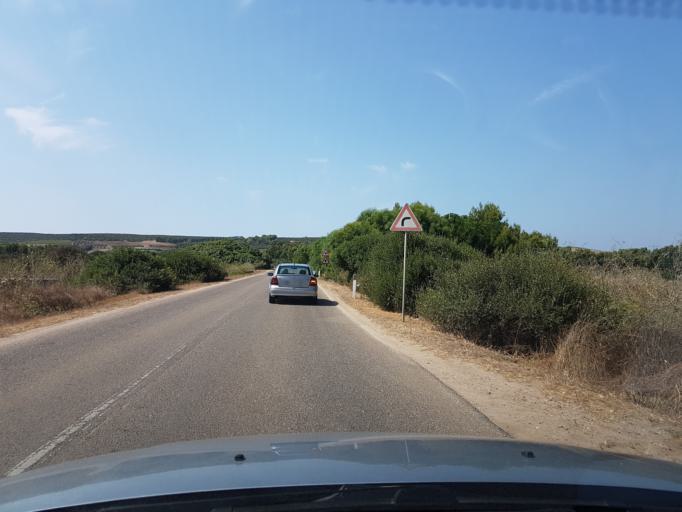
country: IT
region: Sardinia
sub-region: Provincia di Oristano
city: Cabras
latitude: 39.9163
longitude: 8.4522
